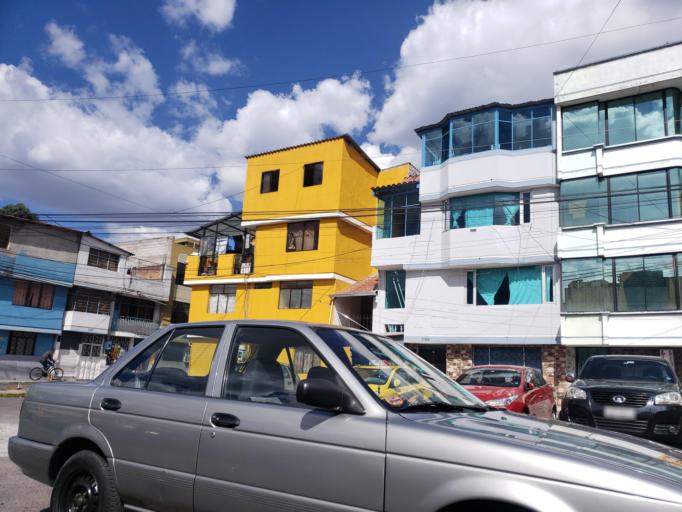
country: EC
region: Pichincha
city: Quito
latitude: -0.2723
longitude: -78.5415
